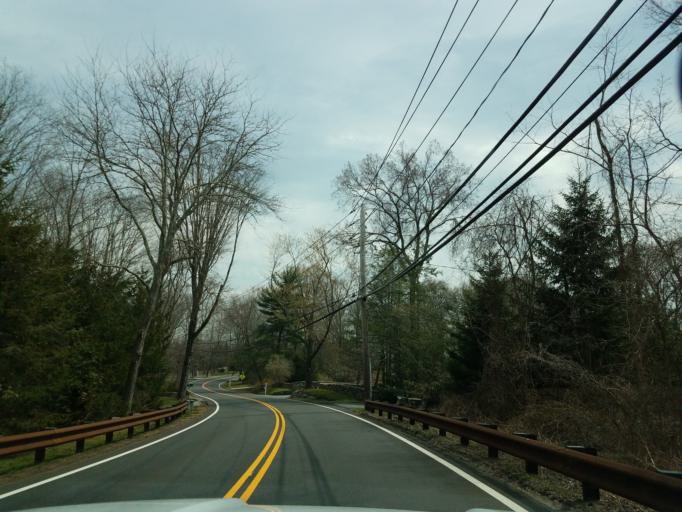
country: US
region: Connecticut
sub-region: Fairfield County
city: Glenville
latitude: 41.0825
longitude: -73.6459
